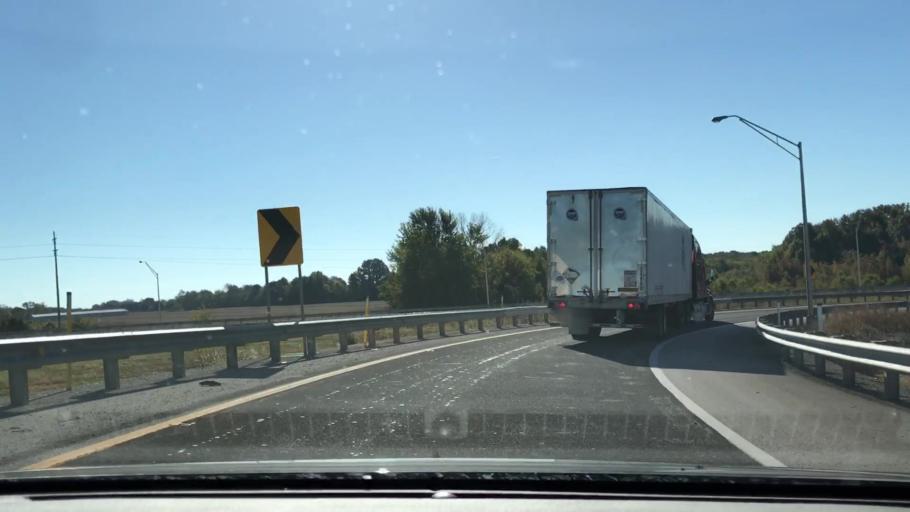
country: US
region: Kentucky
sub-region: Warren County
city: Plano
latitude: 36.9094
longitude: -86.4307
